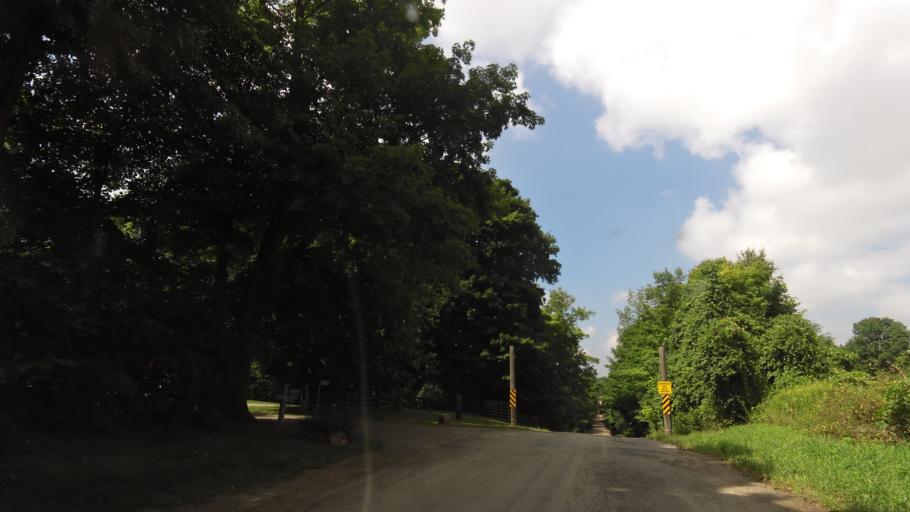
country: CA
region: Ontario
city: Oshawa
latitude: 44.0025
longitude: -78.8771
